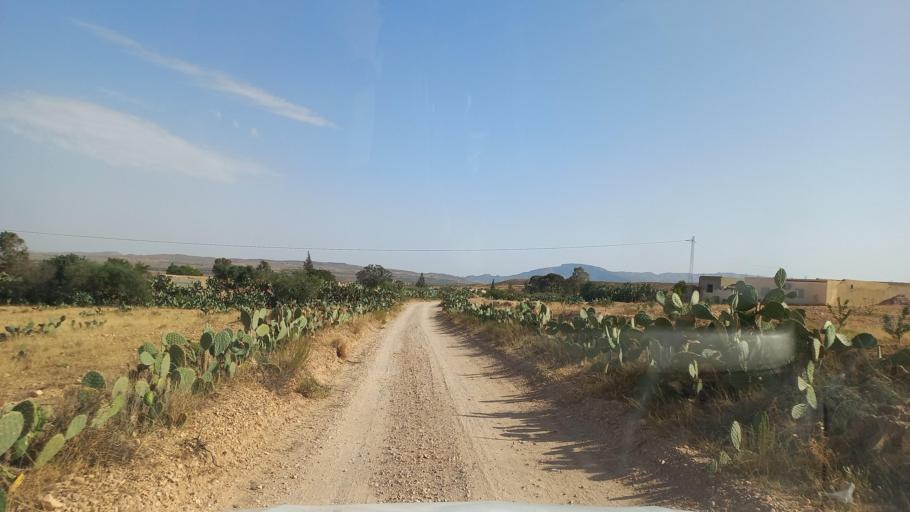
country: TN
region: Al Qasrayn
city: Kasserine
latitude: 35.2541
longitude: 8.9280
